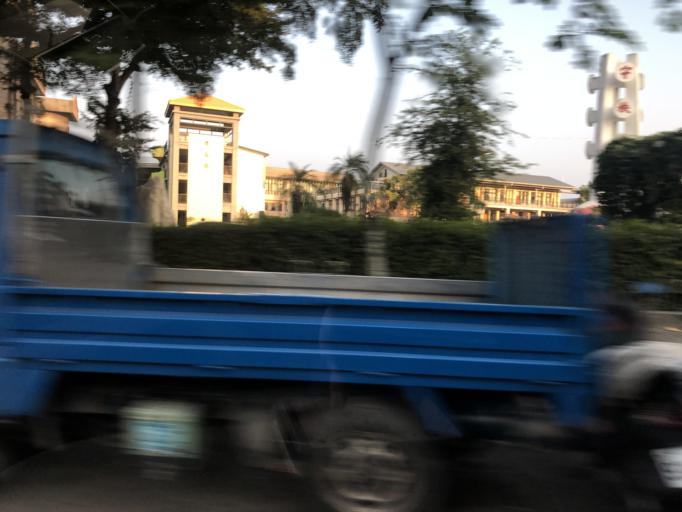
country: TW
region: Taiwan
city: Xinying
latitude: 23.1861
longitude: 120.2528
